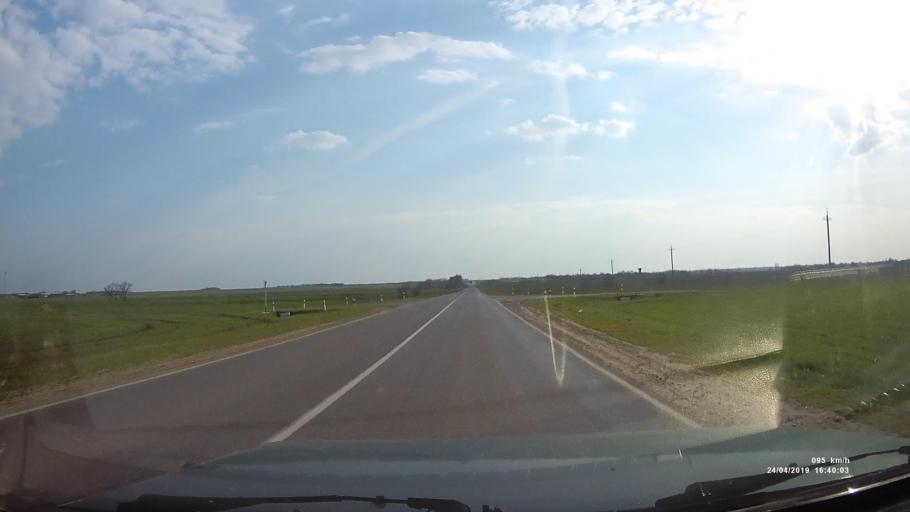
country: RU
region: Rostov
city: Gundorovskiy
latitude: 46.8378
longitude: 41.8863
